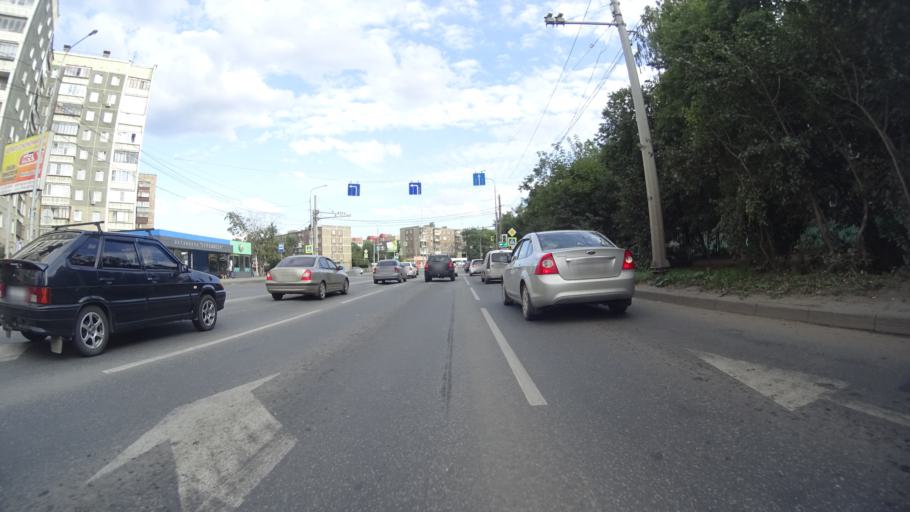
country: RU
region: Chelyabinsk
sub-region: Gorod Chelyabinsk
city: Chelyabinsk
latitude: 55.1990
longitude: 61.3312
